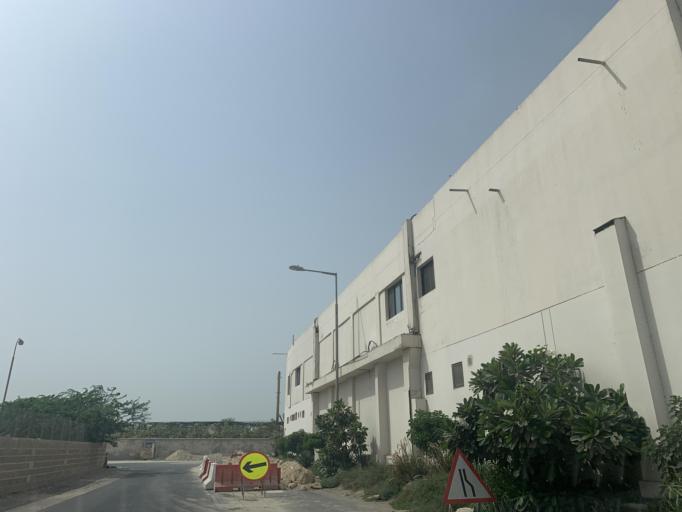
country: BH
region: Manama
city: Jidd Hafs
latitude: 26.2000
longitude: 50.4718
